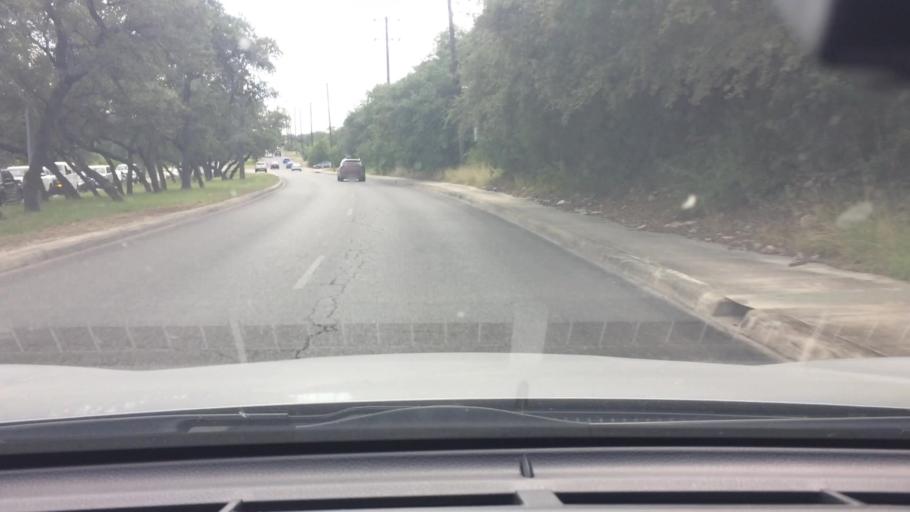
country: US
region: Texas
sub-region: Bexar County
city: Leon Valley
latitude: 29.4770
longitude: -98.6940
